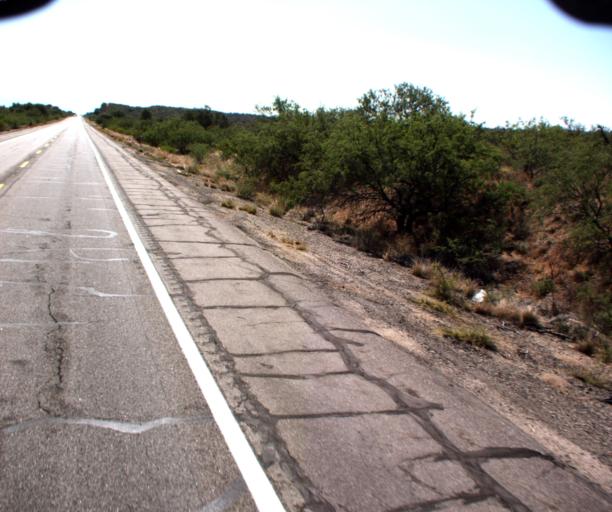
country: US
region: Arizona
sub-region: Pinal County
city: Oracle
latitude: 32.6229
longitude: -110.7805
